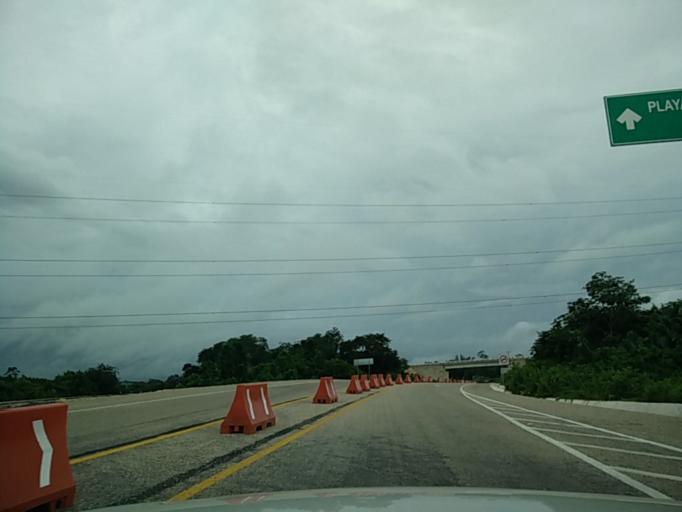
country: MX
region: Quintana Roo
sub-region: Lazaro Cardenas
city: El Tintal
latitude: 20.8942
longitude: -87.4386
